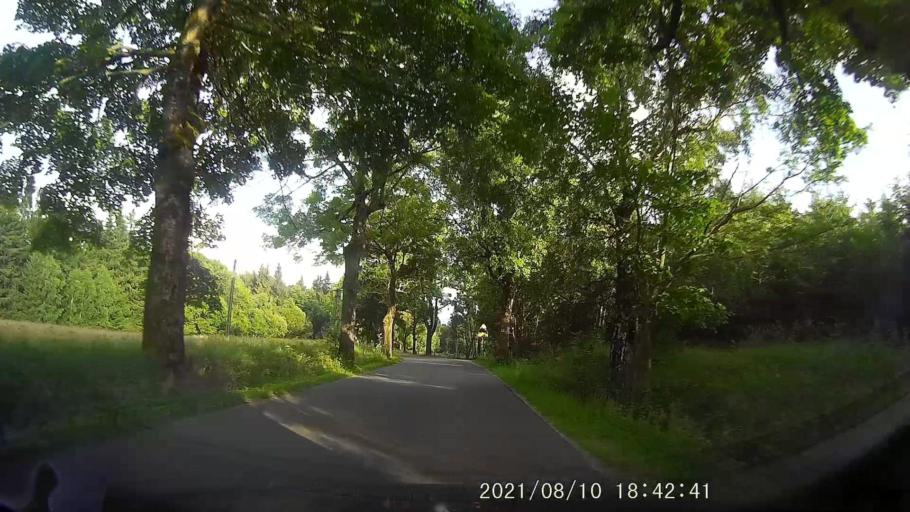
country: PL
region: Lower Silesian Voivodeship
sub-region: Powiat klodzki
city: Duszniki-Zdroj
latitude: 50.4483
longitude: 16.3472
